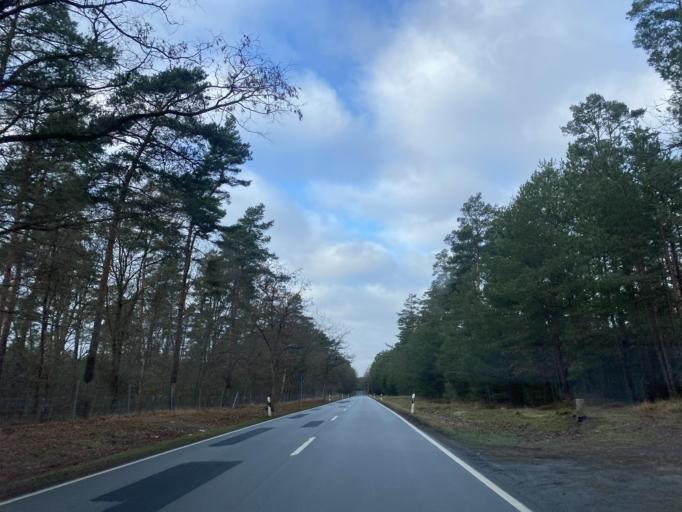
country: DE
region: Saxony
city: Rietschen
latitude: 51.4933
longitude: 14.8294
